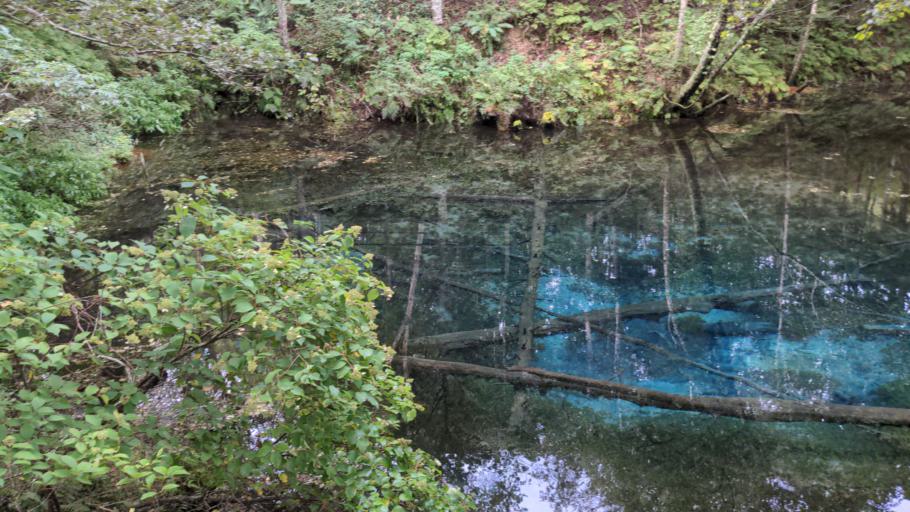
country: JP
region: Hokkaido
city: Abashiri
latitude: 43.6451
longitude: 144.5501
